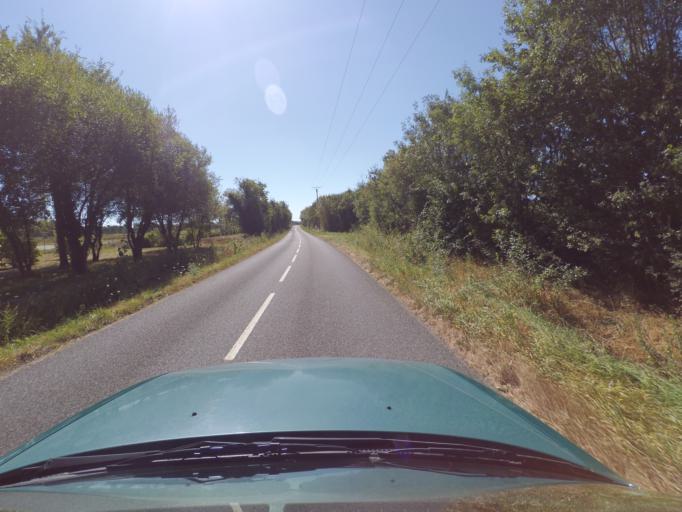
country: FR
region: Pays de la Loire
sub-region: Departement de la Loire-Atlantique
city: Le Bignon
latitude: 47.1169
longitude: -1.5038
